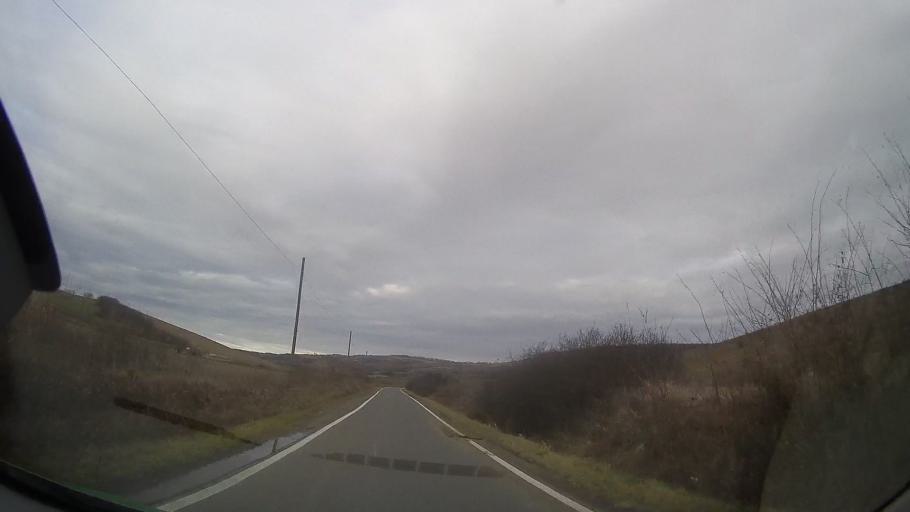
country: RO
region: Mures
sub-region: Comuna Cozma
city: Cozma
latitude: 46.7911
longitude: 24.5435
